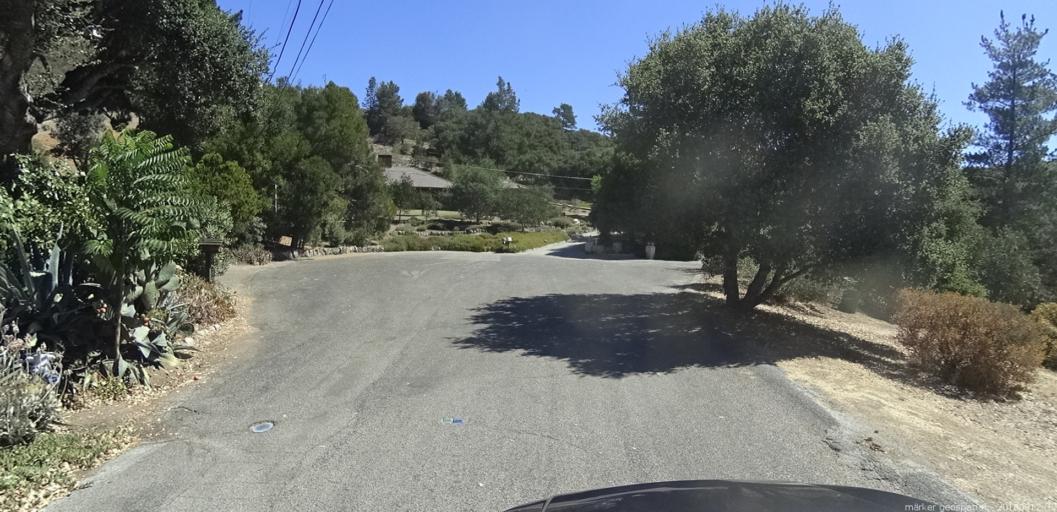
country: US
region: California
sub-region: Monterey County
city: Carmel Valley Village
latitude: 36.4816
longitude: -121.7234
